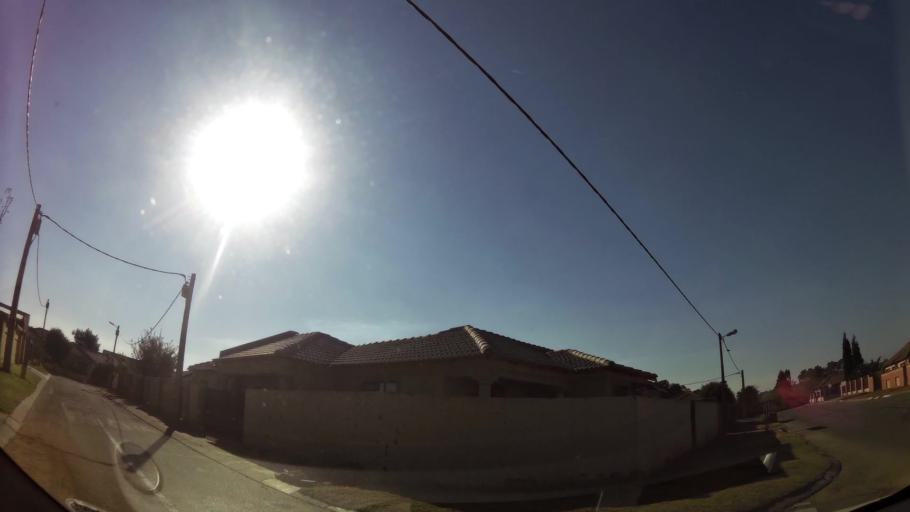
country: ZA
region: Gauteng
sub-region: City of Johannesburg Metropolitan Municipality
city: Johannesburg
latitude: -26.2070
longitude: 27.9717
